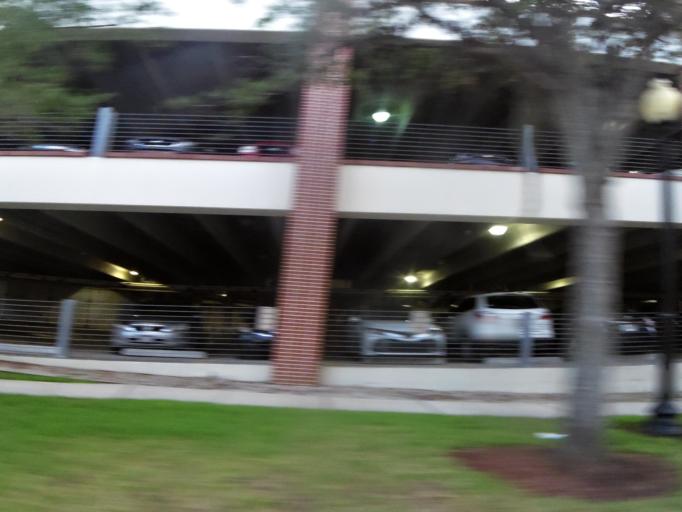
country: US
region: Florida
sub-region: Duval County
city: Jacksonville
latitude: 30.3066
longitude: -81.6907
